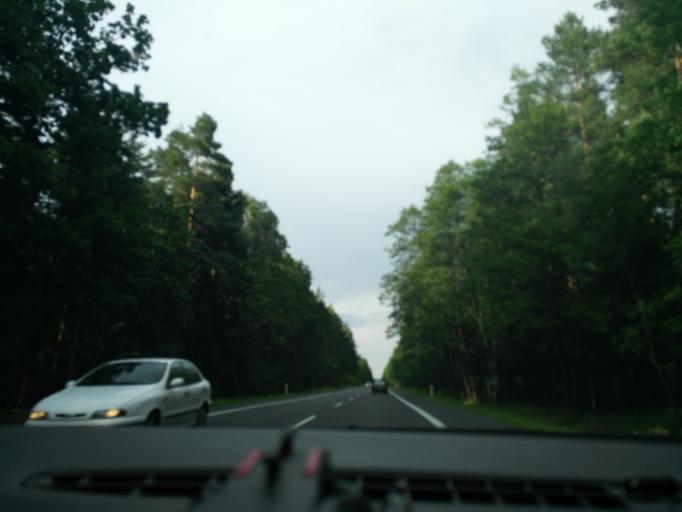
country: PL
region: Subcarpathian Voivodeship
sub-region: Powiat nizanski
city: Zarzecze
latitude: 50.5610
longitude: 22.2438
